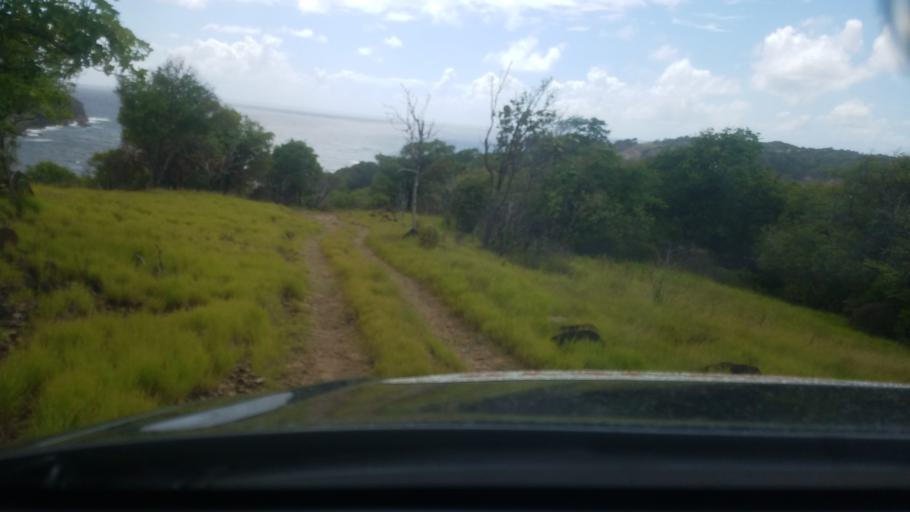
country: LC
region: Praslin
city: Praslin
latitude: 13.8685
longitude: -60.8879
